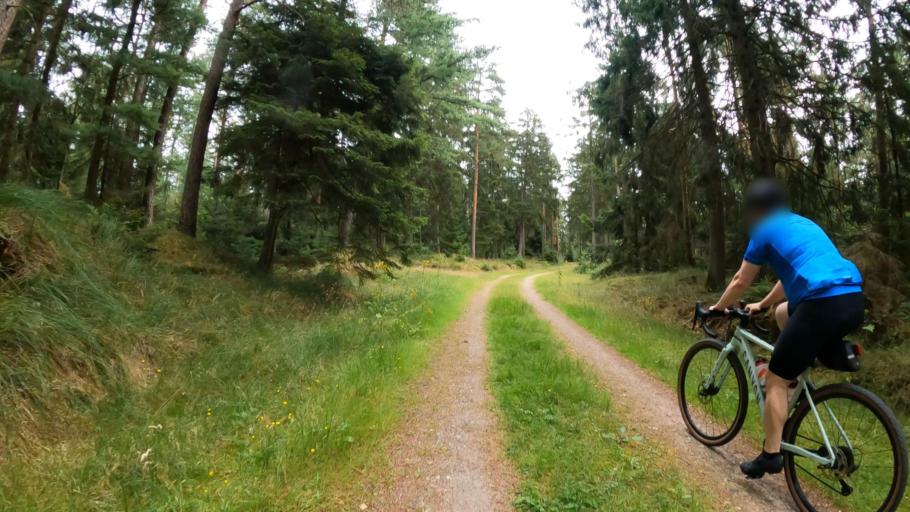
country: DE
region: Schleswig-Holstein
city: Bark
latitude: 53.9307
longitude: 10.1720
